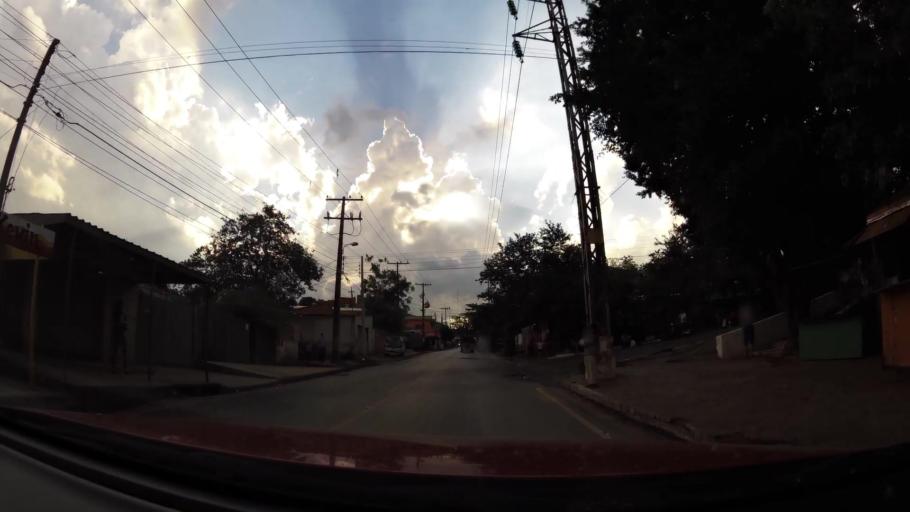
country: PY
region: Central
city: Villa Elisa
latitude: -25.3559
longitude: -57.5681
